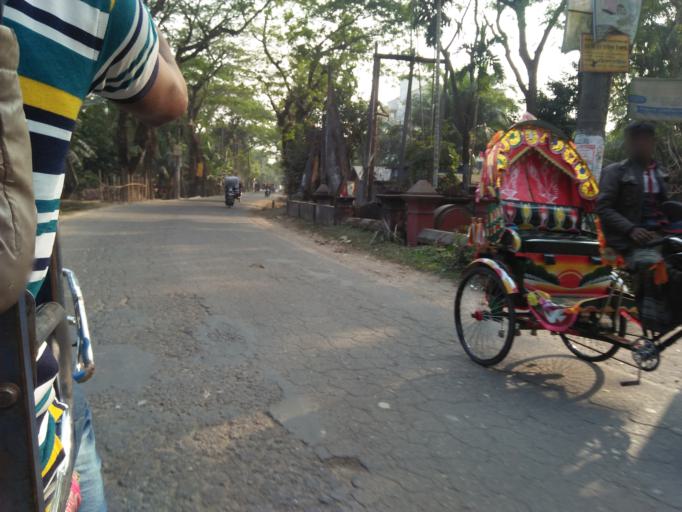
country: BD
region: Barisal
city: Bhola
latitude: 22.6966
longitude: 90.6435
